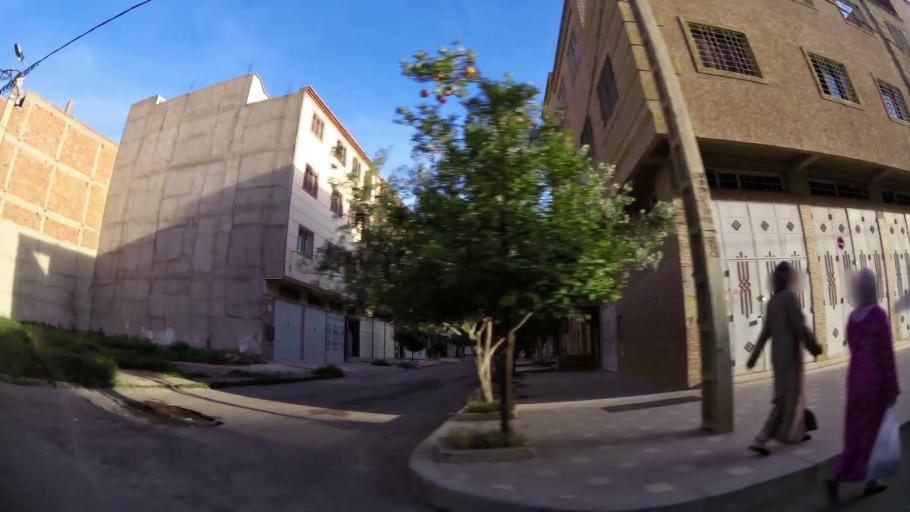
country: MA
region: Oriental
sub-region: Oujda-Angad
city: Oujda
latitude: 34.6777
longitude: -1.8995
